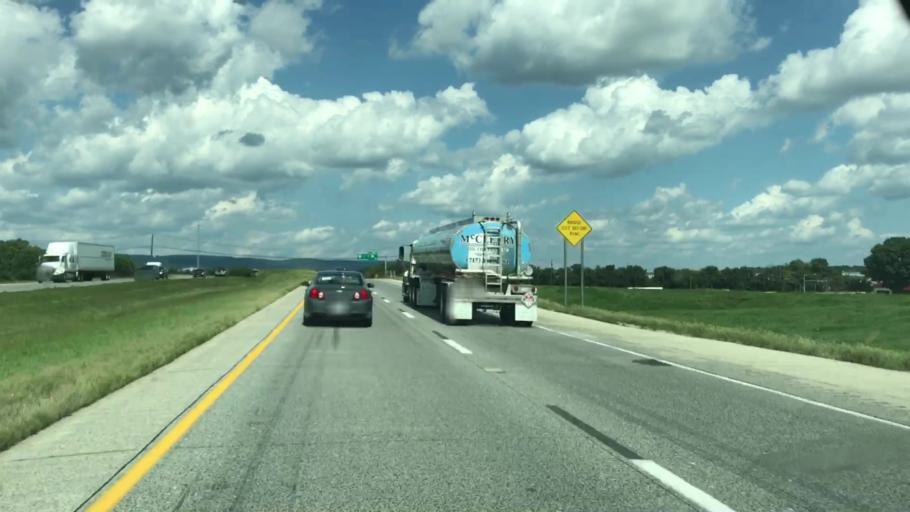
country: US
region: Pennsylvania
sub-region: Cumberland County
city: Schlusser
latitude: 40.2329
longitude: -77.1294
